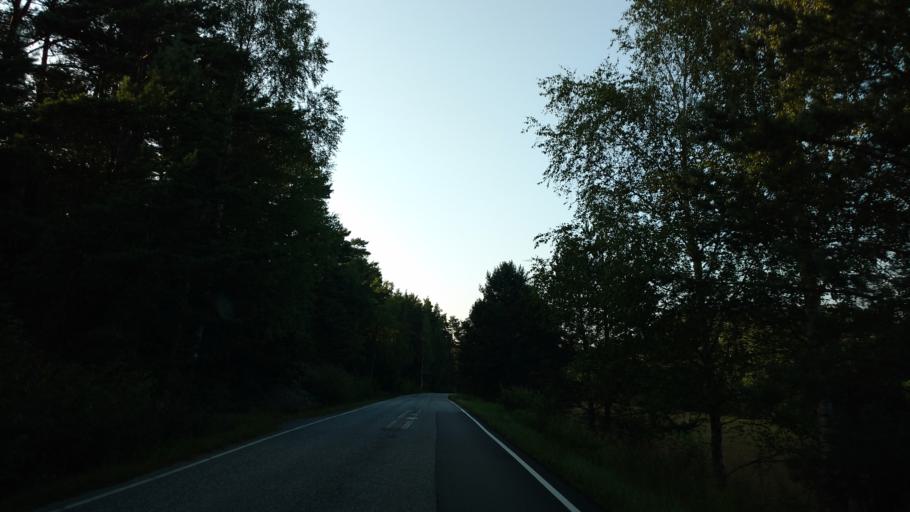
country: FI
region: Varsinais-Suomi
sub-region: Aboland-Turunmaa
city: Dragsfjaerd
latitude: 60.0209
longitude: 22.4592
